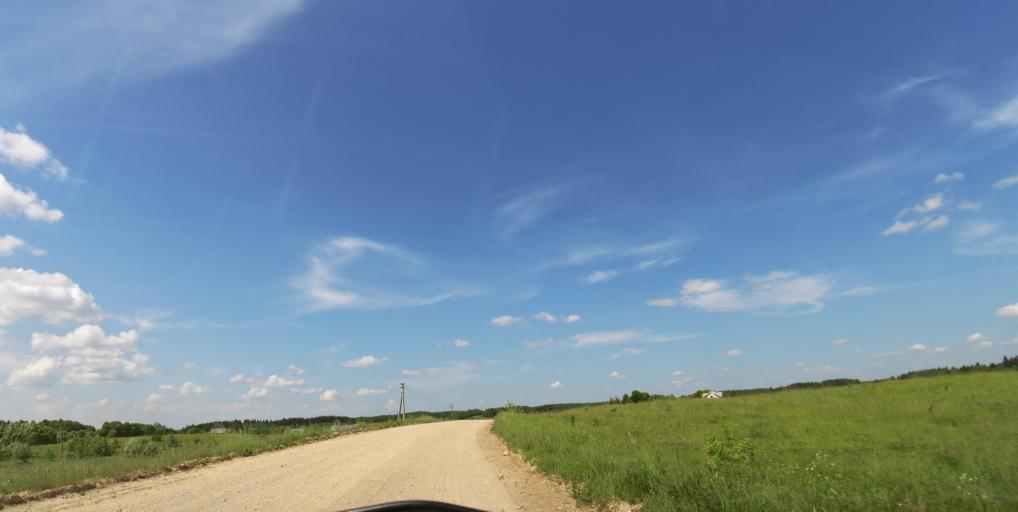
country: LT
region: Vilnius County
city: Pilaite
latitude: 54.7457
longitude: 25.1307
